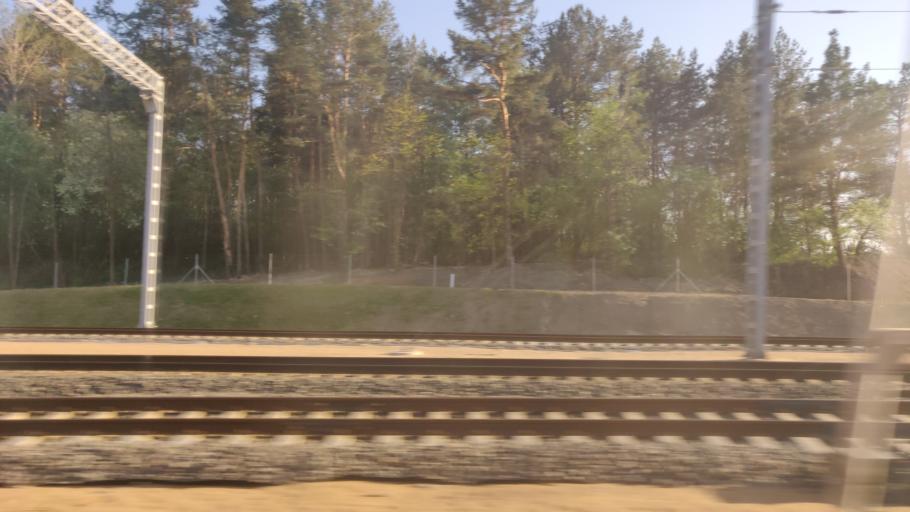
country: LT
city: Baltoji Voke
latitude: 54.6311
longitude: 25.1468
